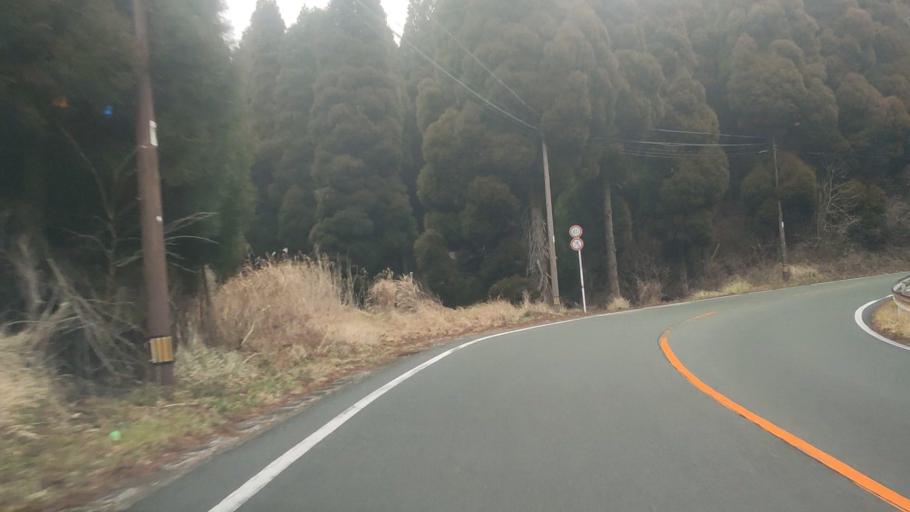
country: JP
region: Kumamoto
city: Aso
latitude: 32.8779
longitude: 131.1727
